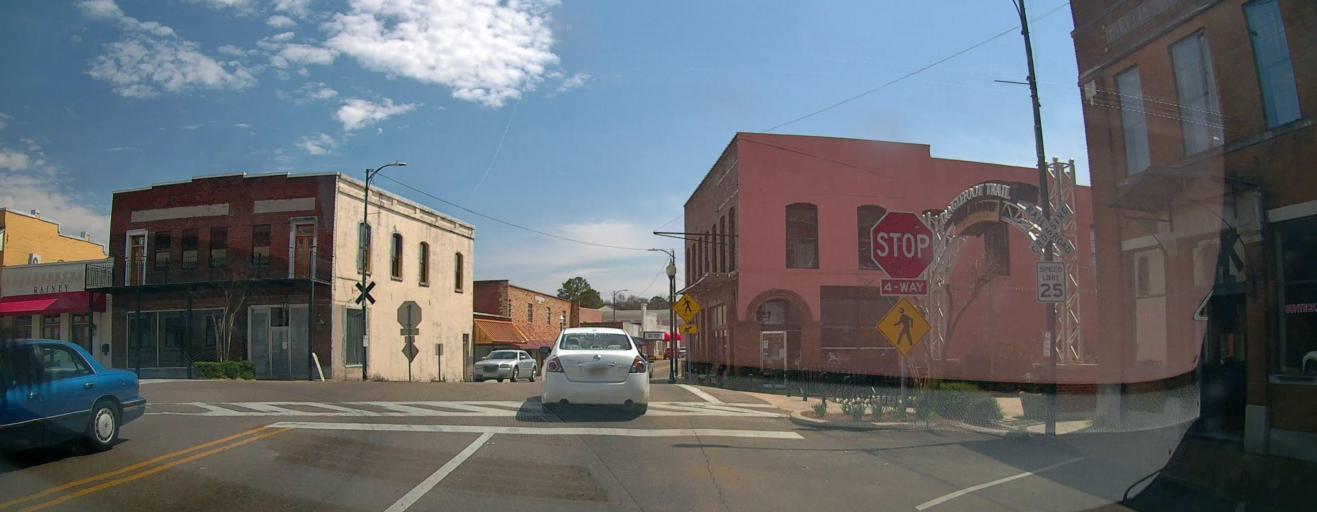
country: US
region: Mississippi
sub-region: Union County
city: New Albany
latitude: 34.4939
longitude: -89.0086
